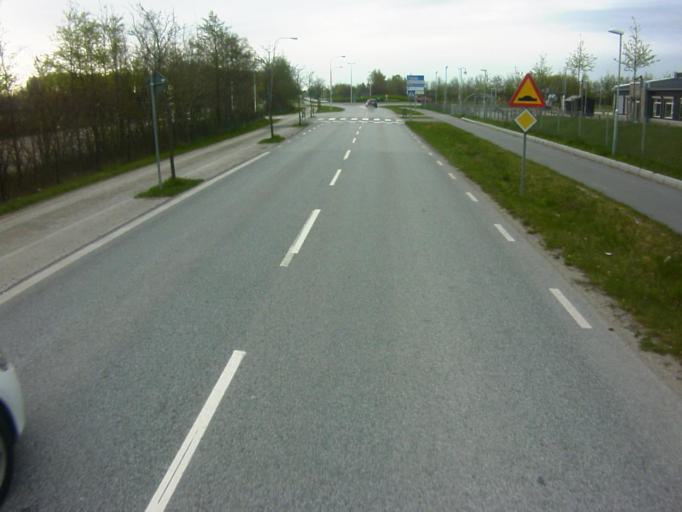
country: SE
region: Skane
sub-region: Kavlinge Kommun
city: Loddekopinge
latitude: 55.7678
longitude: 13.0122
